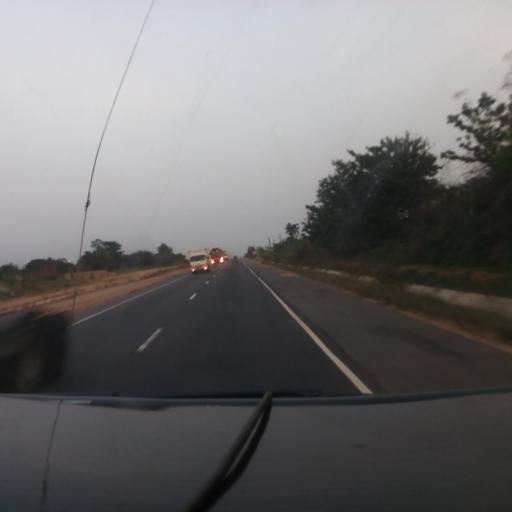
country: GH
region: Eastern
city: Nsawam
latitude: 5.8814
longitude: -0.3751
